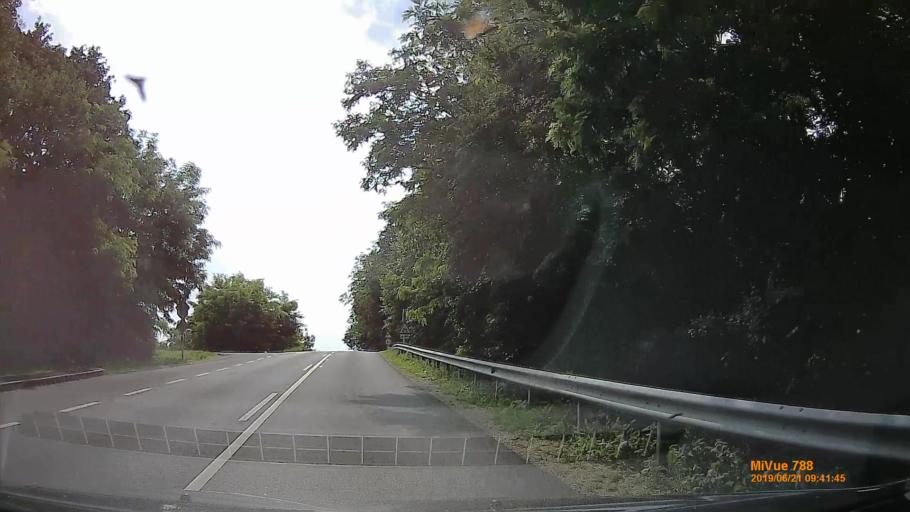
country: HU
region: Somogy
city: Taszar
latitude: 46.2931
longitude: 17.9614
